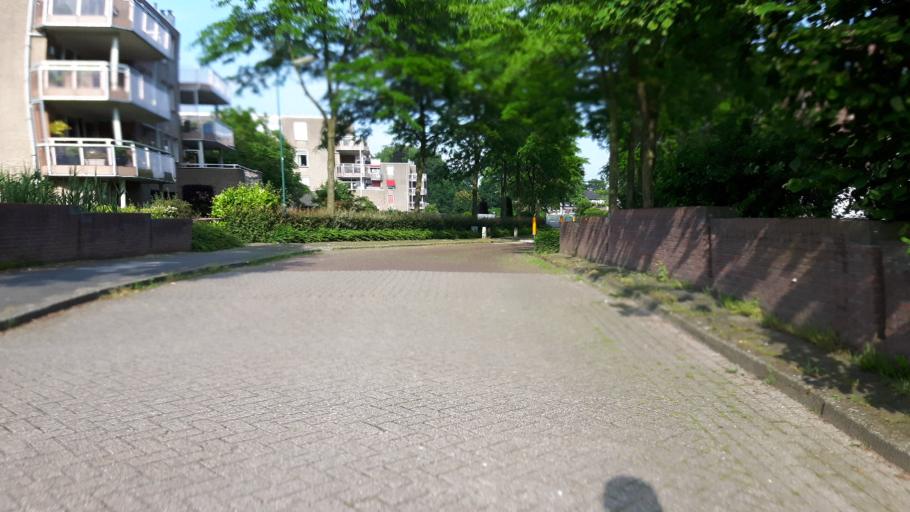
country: NL
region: Utrecht
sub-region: Gemeente Woerden
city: Woerden
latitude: 52.0933
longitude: 4.8969
